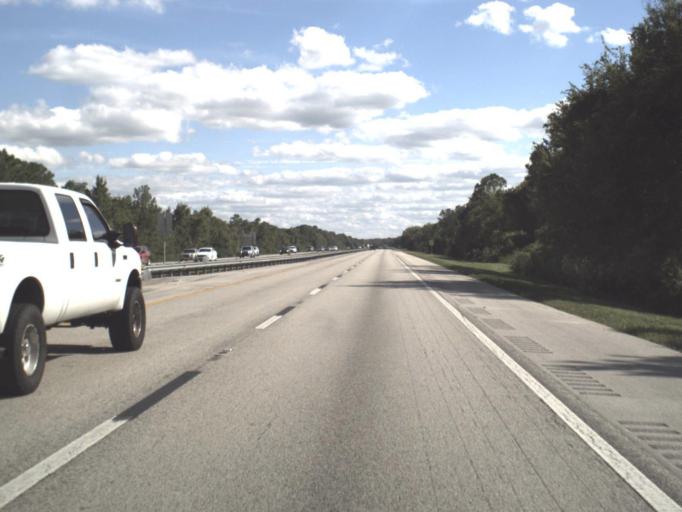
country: US
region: Florida
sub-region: Indian River County
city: Fellsmere
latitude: 27.5870
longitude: -80.8121
